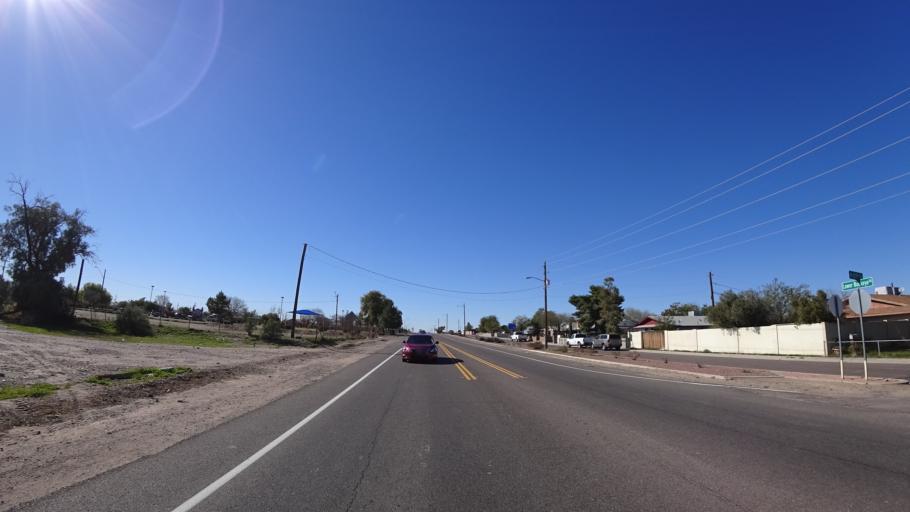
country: US
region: Arizona
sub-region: Maricopa County
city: Avondale
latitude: 33.4204
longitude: -112.3255
